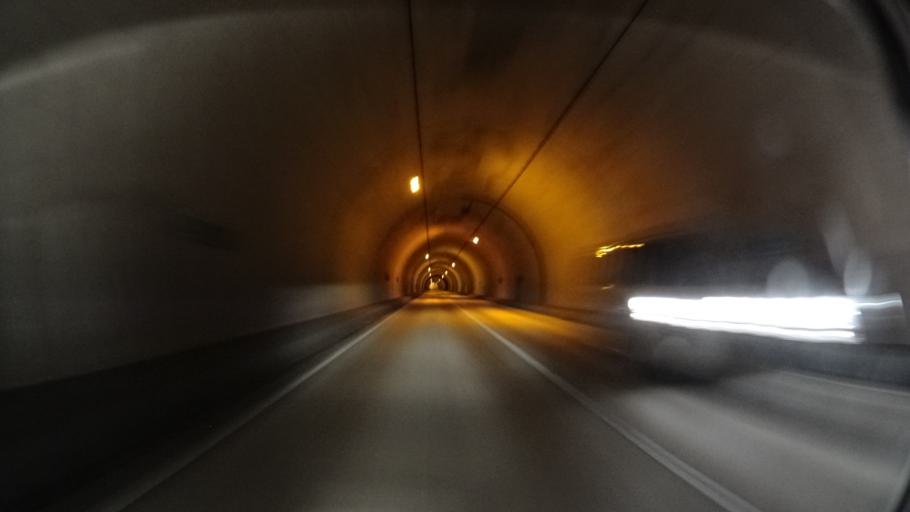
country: JP
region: Hyogo
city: Toyooka
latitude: 35.5010
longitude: 134.9079
